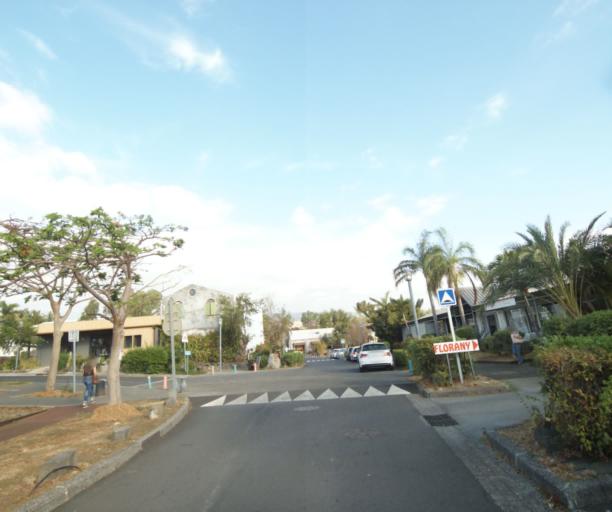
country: RE
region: Reunion
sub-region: Reunion
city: Saint-Paul
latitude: -21.0451
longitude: 55.2551
